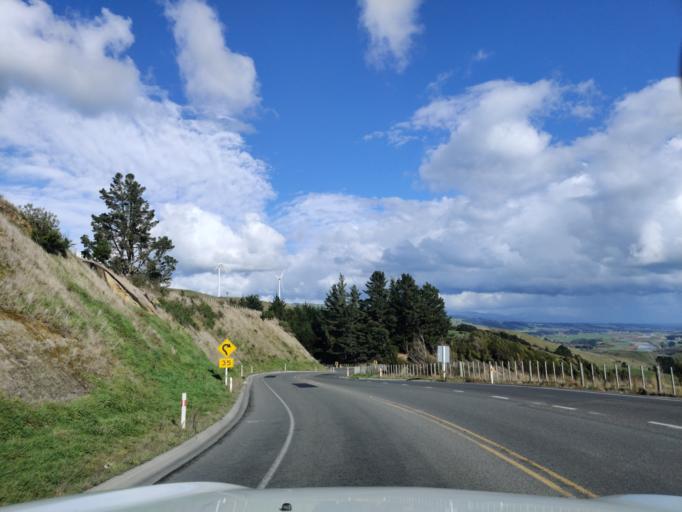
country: NZ
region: Manawatu-Wanganui
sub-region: Palmerston North City
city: Palmerston North
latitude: -40.2866
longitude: 175.7869
